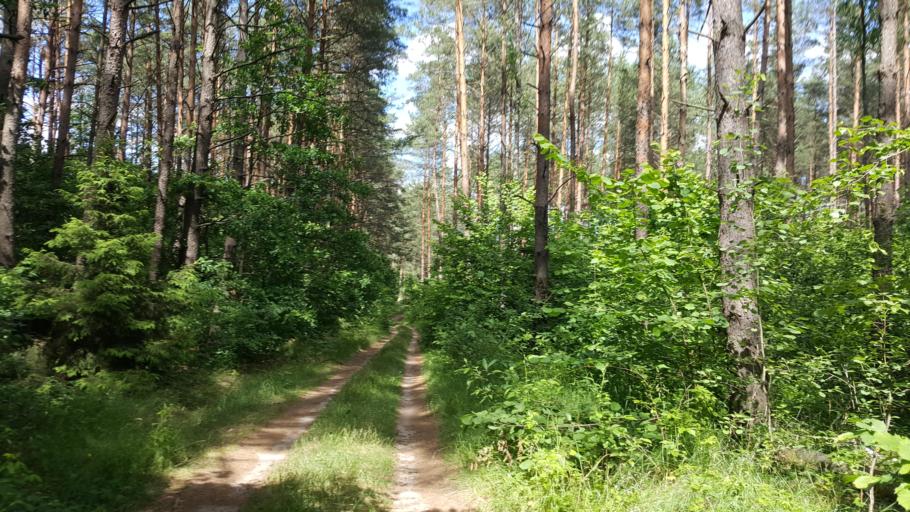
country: PL
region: Podlasie
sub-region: Powiat hajnowski
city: Czeremcha
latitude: 52.5431
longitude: 23.4983
